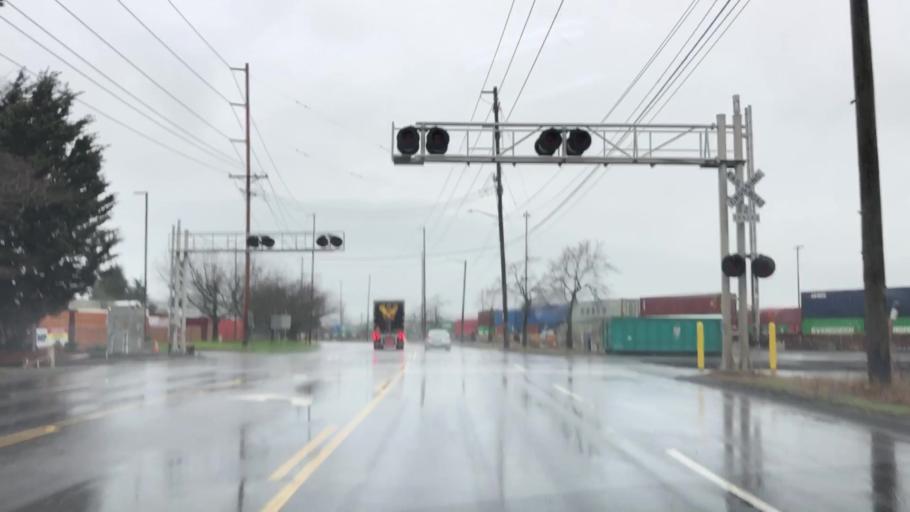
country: US
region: Washington
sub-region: Pierce County
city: Tacoma
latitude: 47.2493
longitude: -122.4007
